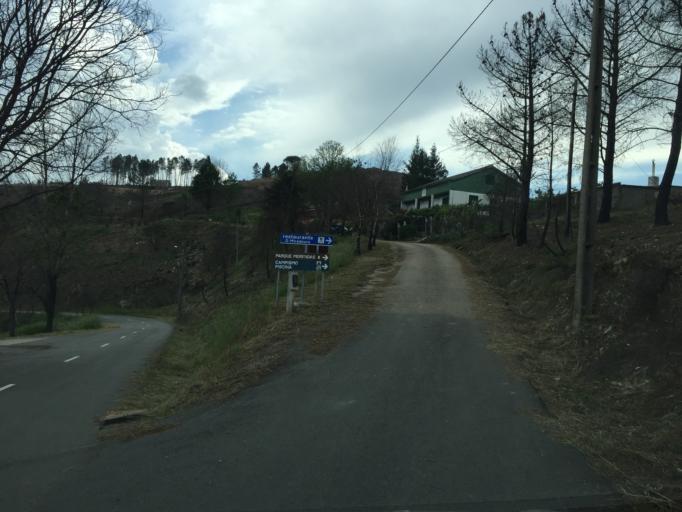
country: PT
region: Coimbra
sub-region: Arganil
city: Arganil
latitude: 40.1651
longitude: -7.9741
